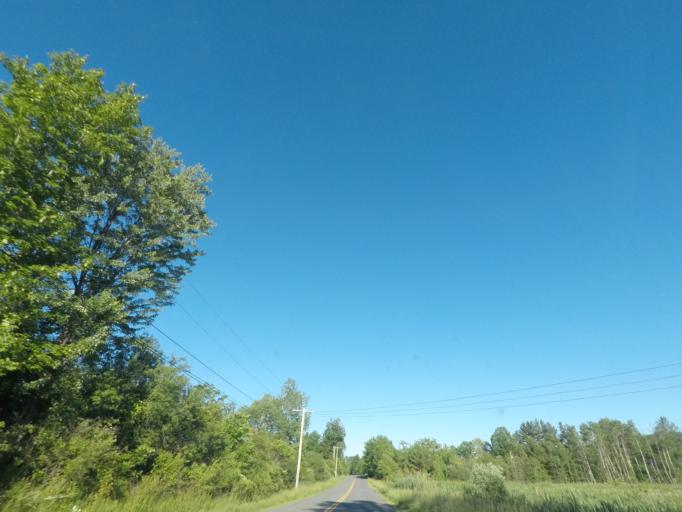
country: US
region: New York
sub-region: Rensselaer County
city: Averill Park
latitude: 42.5805
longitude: -73.5474
